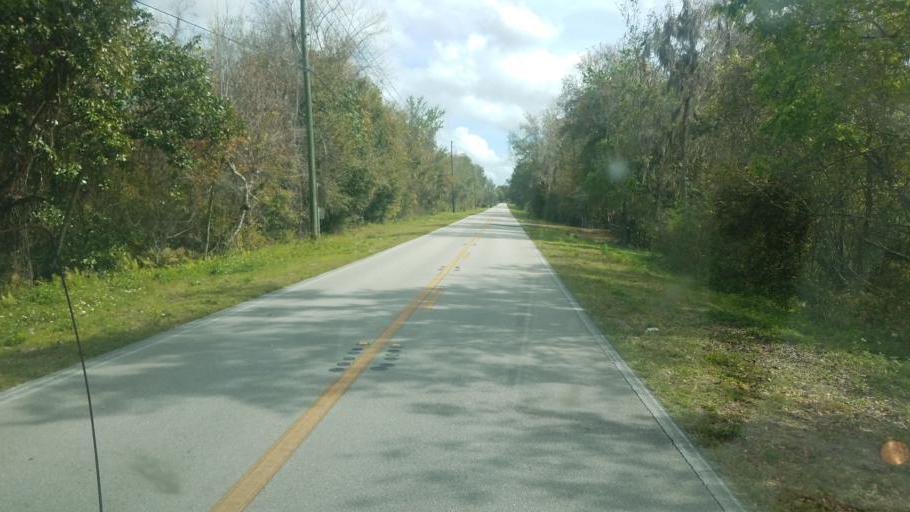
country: US
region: Florida
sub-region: Polk County
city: Dundee
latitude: 28.0556
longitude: -81.5401
